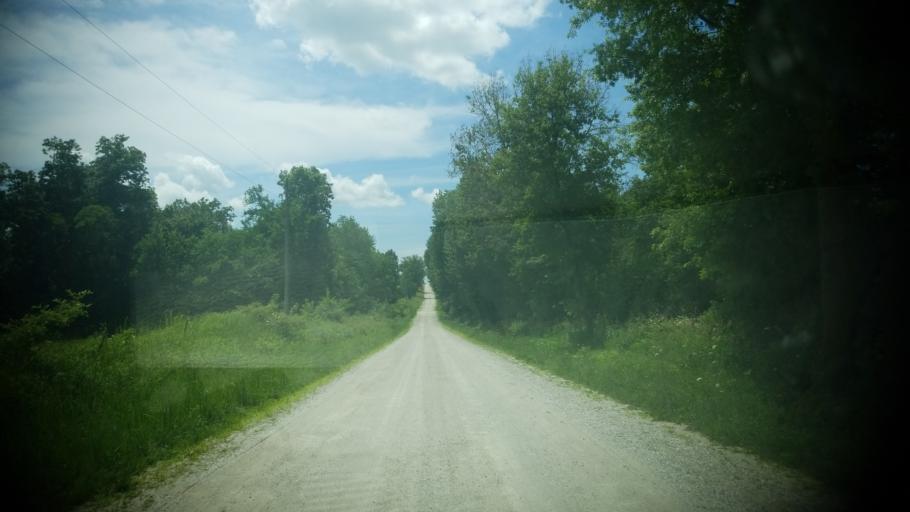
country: US
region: Missouri
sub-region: Pike County
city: Bowling Green
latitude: 39.3088
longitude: -91.3274
